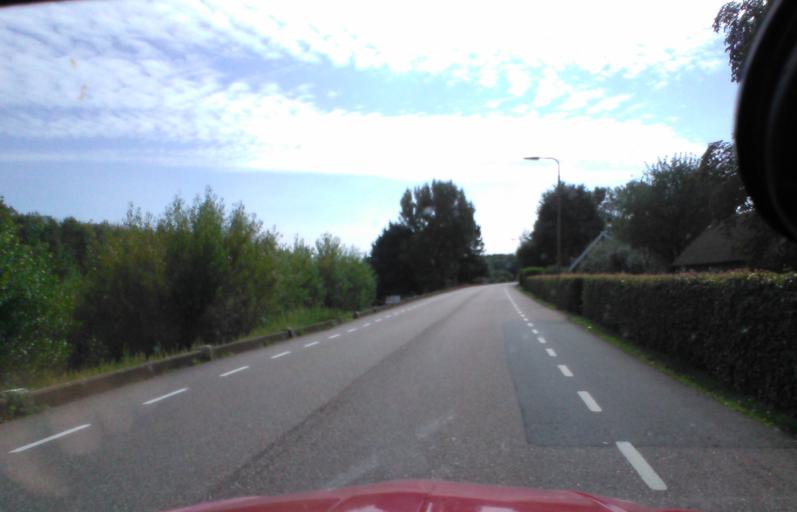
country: NL
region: South Holland
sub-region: Gemeente Gorinchem
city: Gorinchem
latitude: 51.8538
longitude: 4.9948
